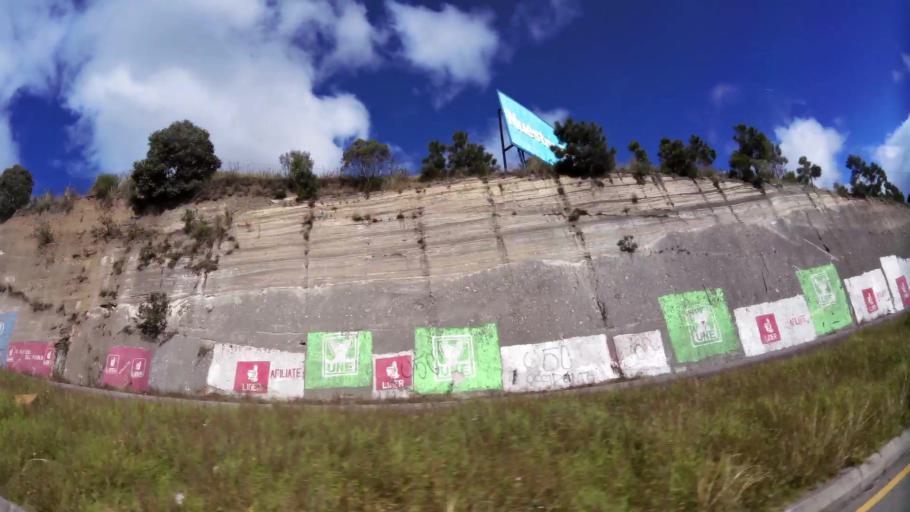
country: GT
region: Quetzaltenango
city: Salcaja
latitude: 14.8956
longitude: -91.4611
